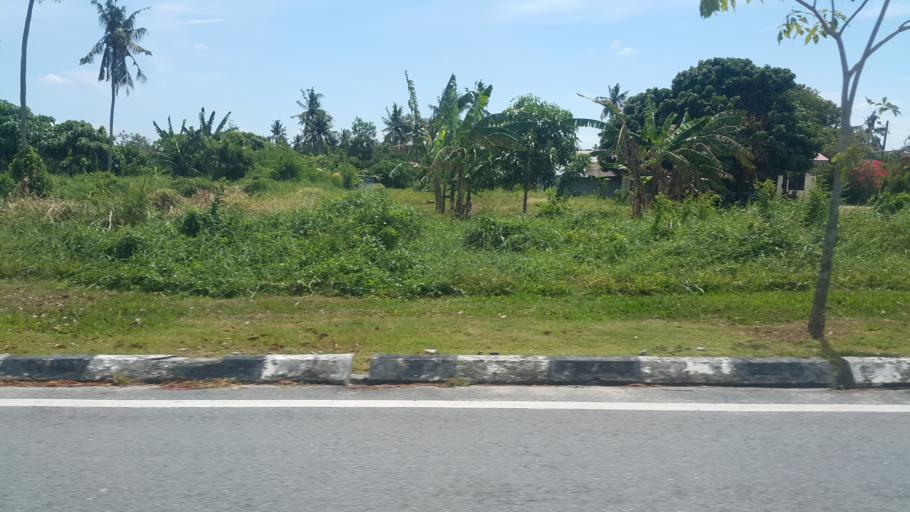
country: MY
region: Melaka
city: Kampung Bukit Baharu
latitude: 2.1875
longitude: 102.2779
